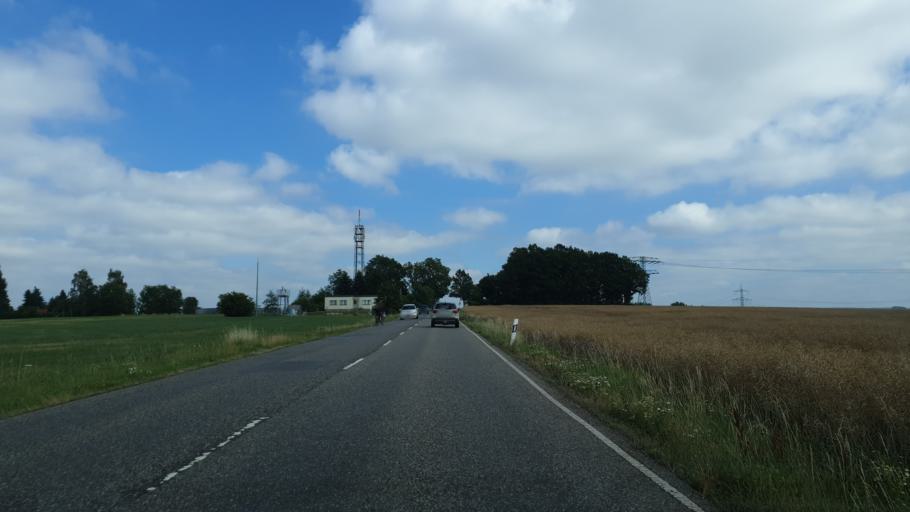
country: DE
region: Saxony
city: Neukirchen
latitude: 50.7920
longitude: 12.8702
